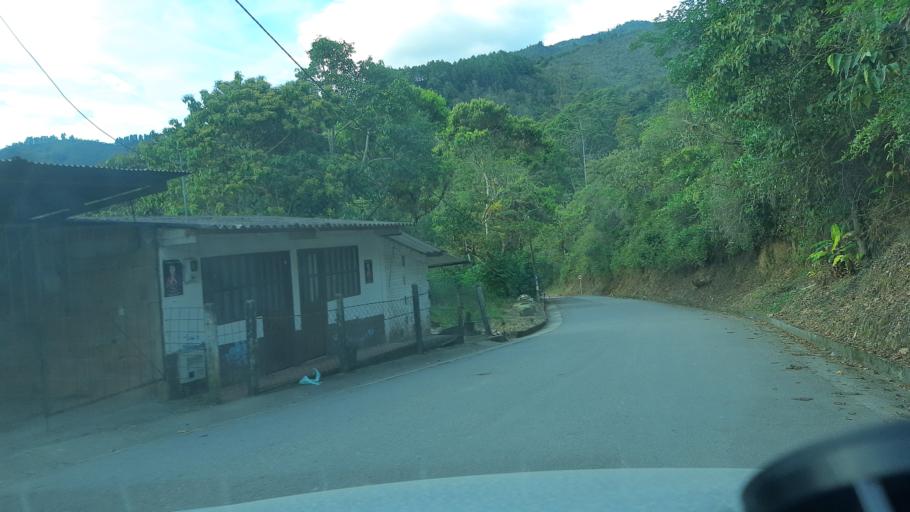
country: CO
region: Boyaca
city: Chivor
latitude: 4.9736
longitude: -73.3226
